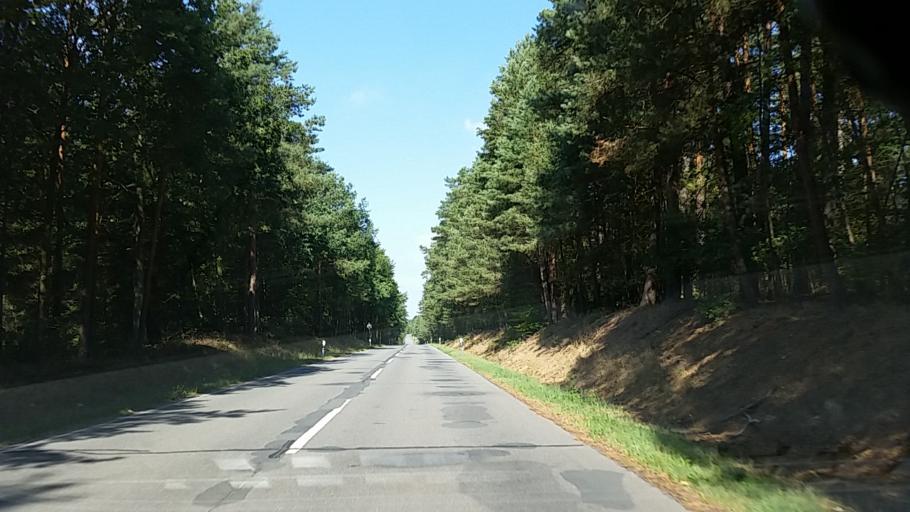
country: DE
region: Lower Saxony
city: Jelmstorf
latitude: 53.1199
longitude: 10.5402
